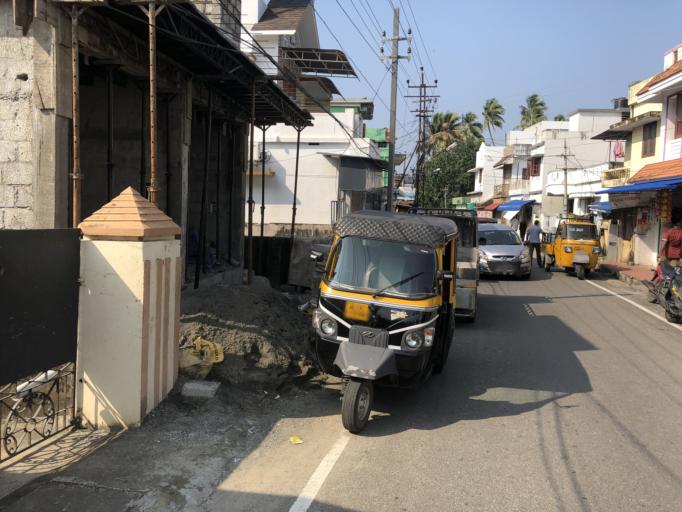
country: IN
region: Kerala
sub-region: Ernakulam
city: Cochin
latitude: 9.9599
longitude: 76.2532
